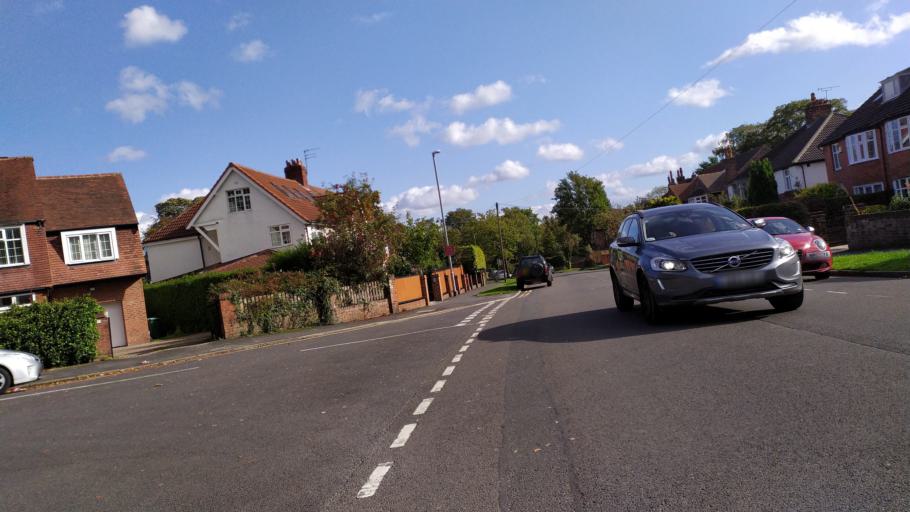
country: GB
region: England
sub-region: City and Borough of Leeds
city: Chapel Allerton
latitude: 53.8257
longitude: -1.5834
